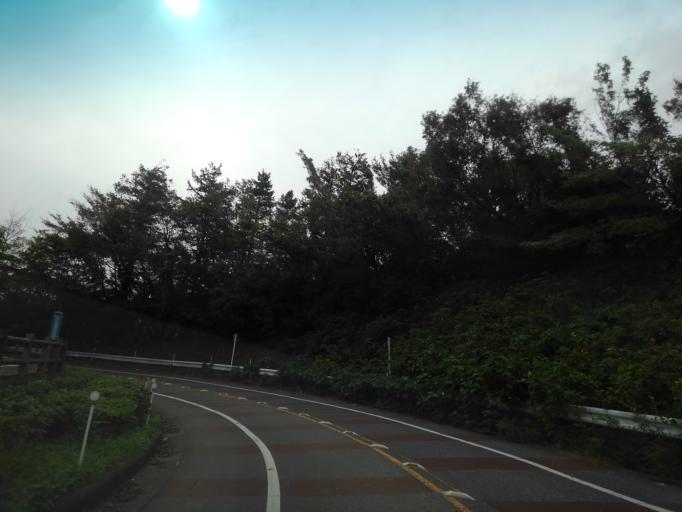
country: JP
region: Tokyo
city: Higashimurayama-shi
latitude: 35.7665
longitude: 139.4178
